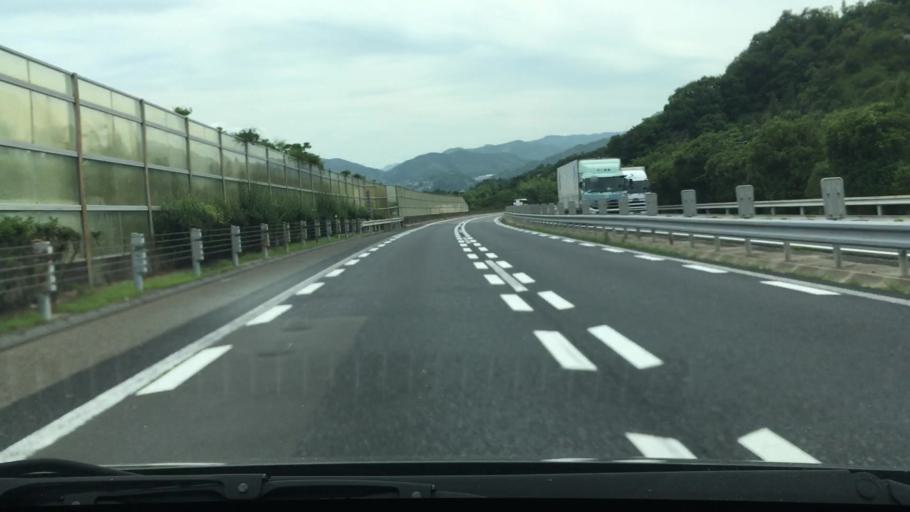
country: JP
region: Hiroshima
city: Ono-hara
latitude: 34.2675
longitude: 132.2423
